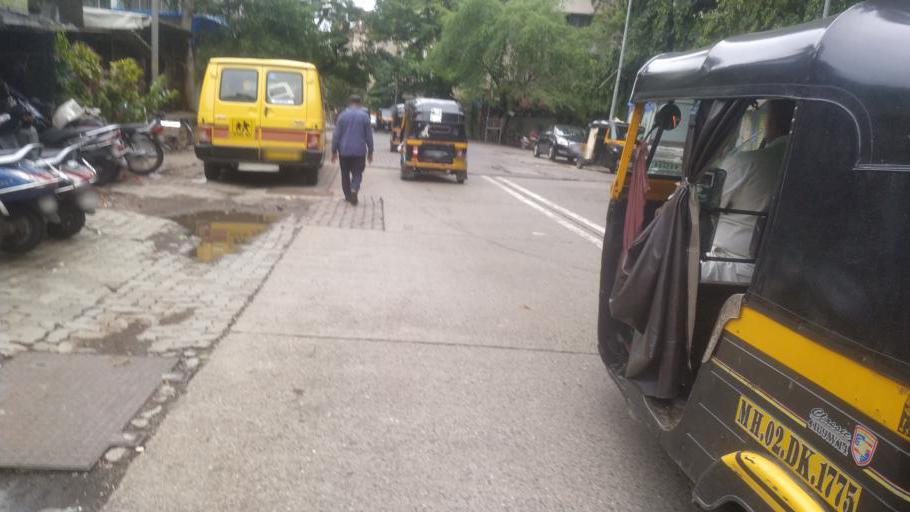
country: IN
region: Maharashtra
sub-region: Mumbai Suburban
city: Mumbai
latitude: 19.0681
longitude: 72.8300
